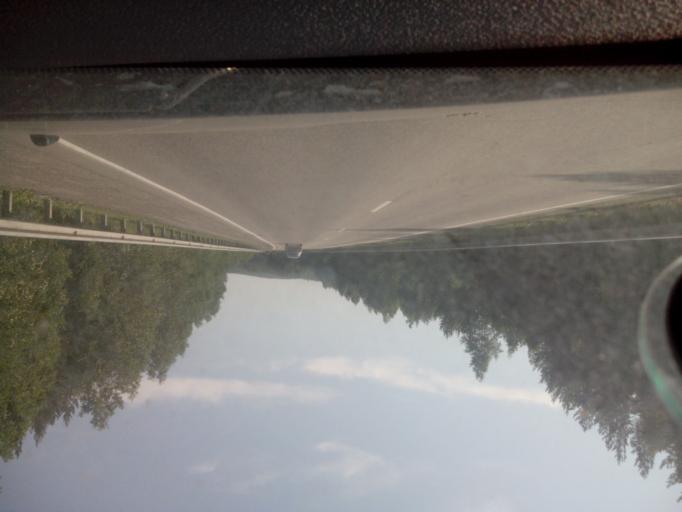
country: RU
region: Sverdlovsk
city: Sredneuralsk
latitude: 57.0746
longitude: 60.4092
